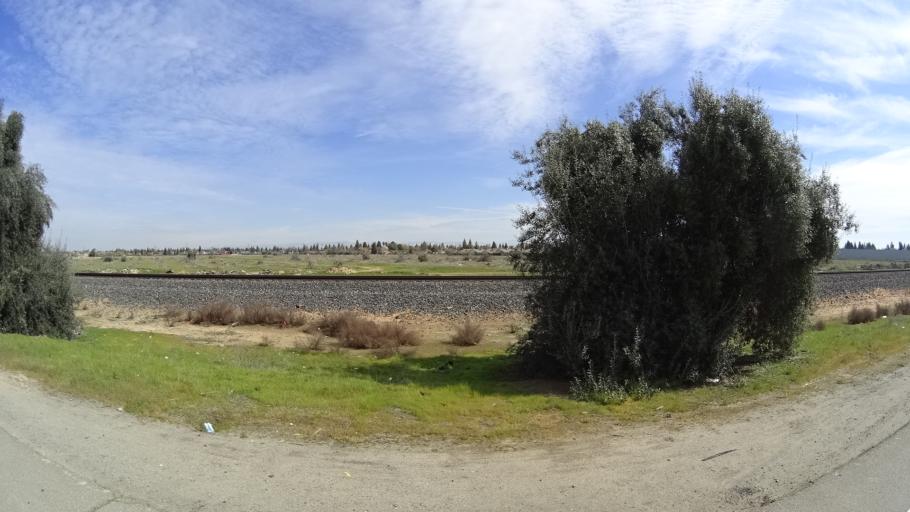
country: US
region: California
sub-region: Fresno County
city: Biola
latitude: 36.8232
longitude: -119.8992
